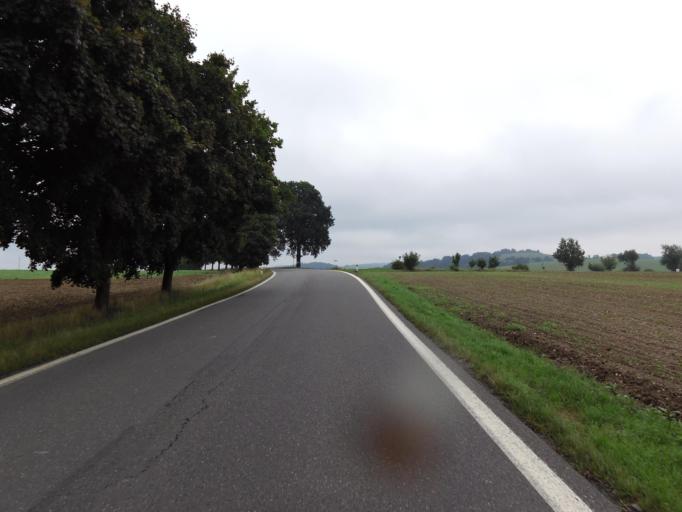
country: CZ
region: Jihocesky
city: Mlada Vozice
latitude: 49.4746
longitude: 14.7857
